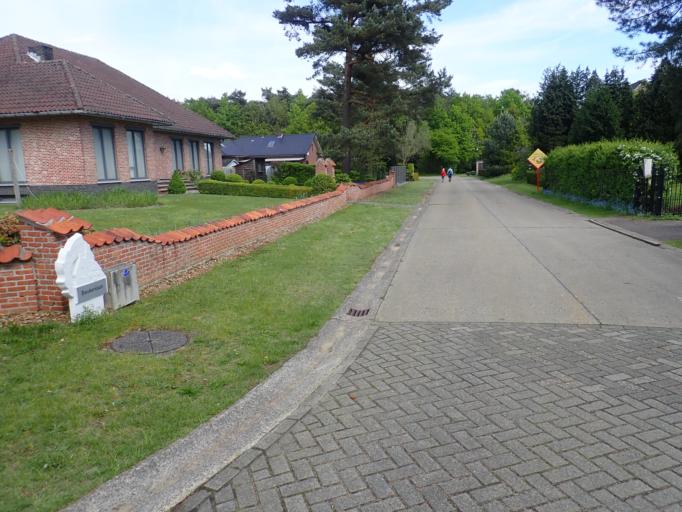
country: BE
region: Flanders
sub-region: Provincie Antwerpen
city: Lille
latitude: 51.2277
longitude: 4.8189
